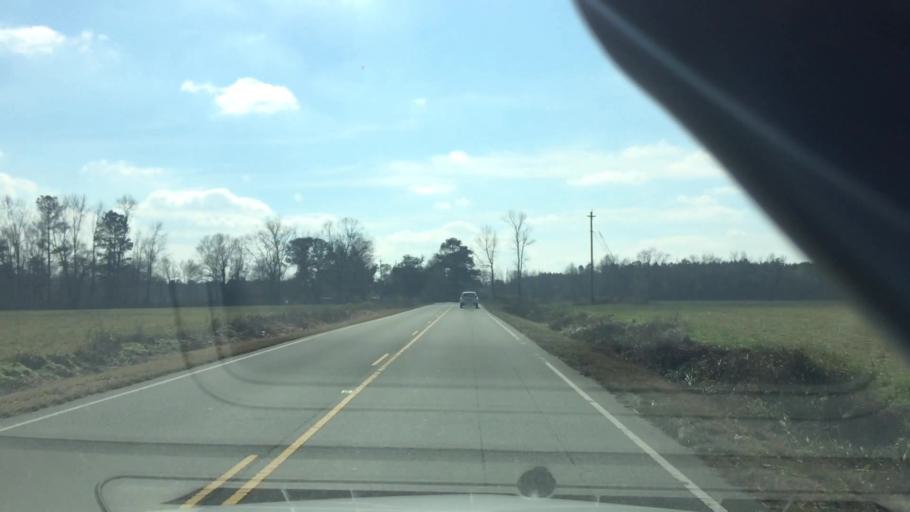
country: US
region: North Carolina
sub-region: Duplin County
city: Beulaville
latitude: 34.8588
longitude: -77.7967
